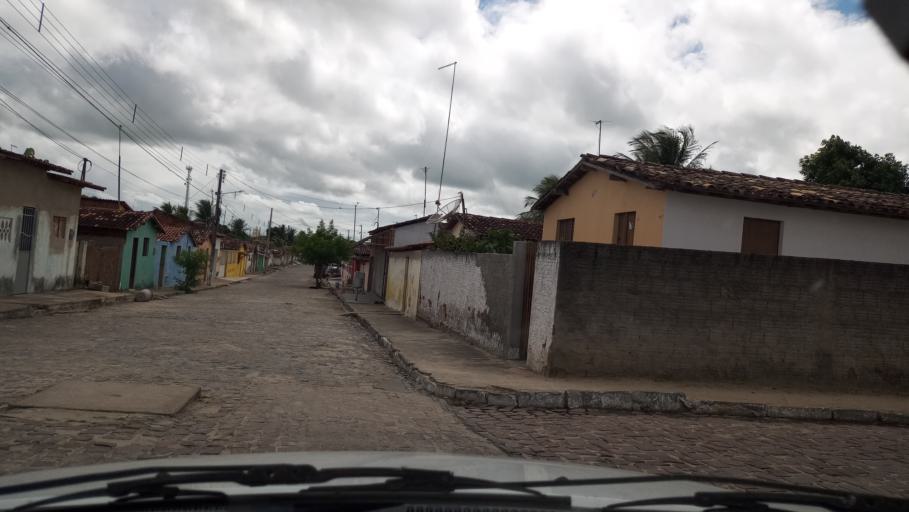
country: BR
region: Rio Grande do Norte
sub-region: Brejinho
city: Brejinho
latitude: -6.1533
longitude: -35.4369
